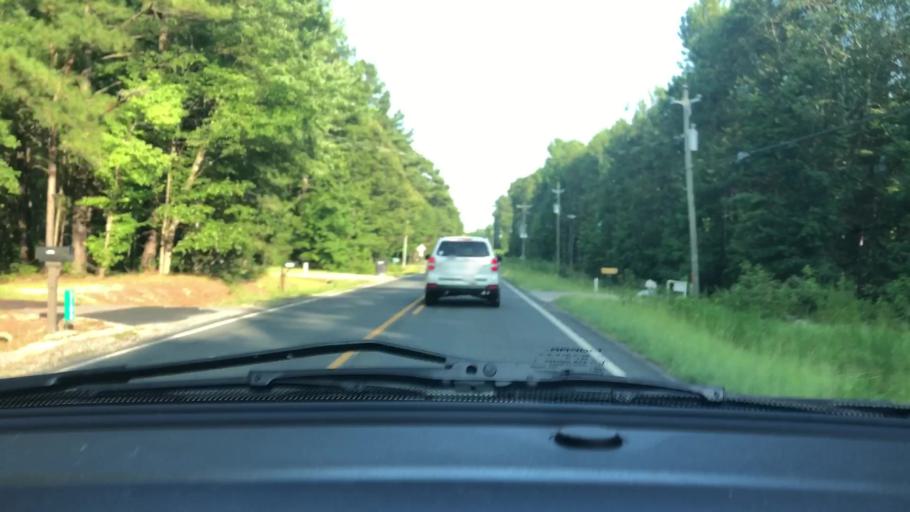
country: US
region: North Carolina
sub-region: Lee County
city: Broadway
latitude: 35.3597
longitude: -79.0843
